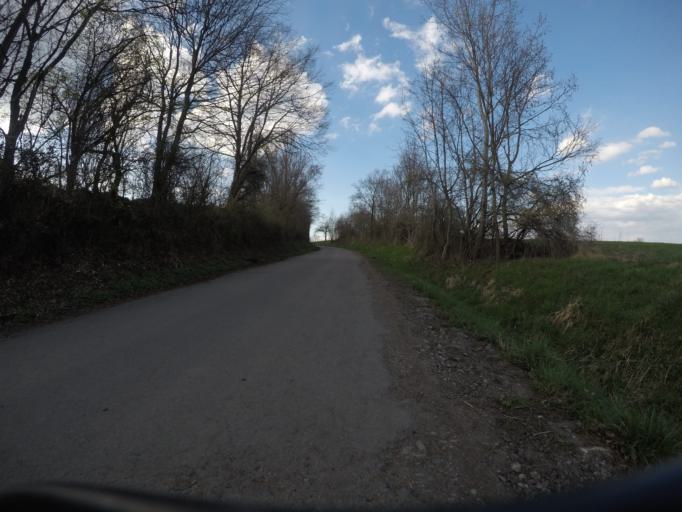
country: DE
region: Baden-Wuerttemberg
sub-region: Tuebingen Region
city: Ofterdingen
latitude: 48.4264
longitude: 9.0310
